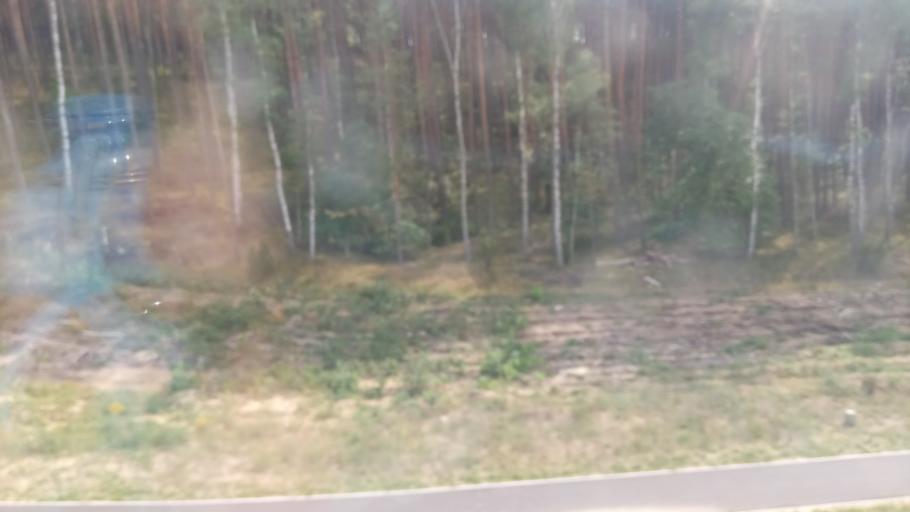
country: PL
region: Greater Poland Voivodeship
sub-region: Powiat pilski
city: Kaczory
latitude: 53.1114
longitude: 16.8490
